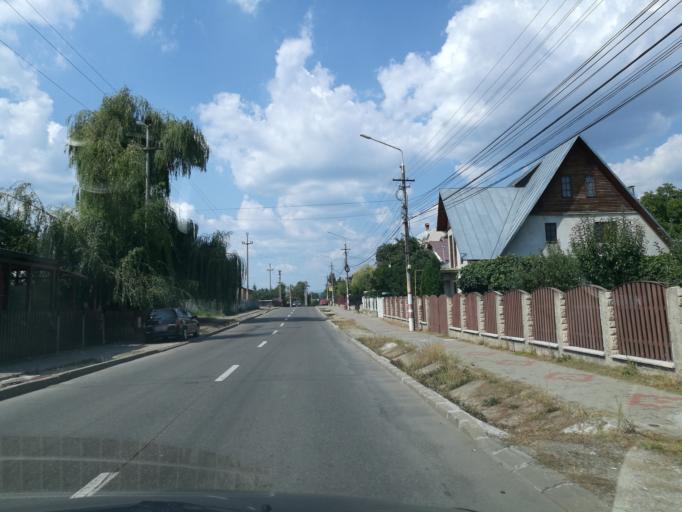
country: RO
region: Neamt
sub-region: Oras Targu Neamt
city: Humulesti
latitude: 47.2085
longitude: 26.3519
